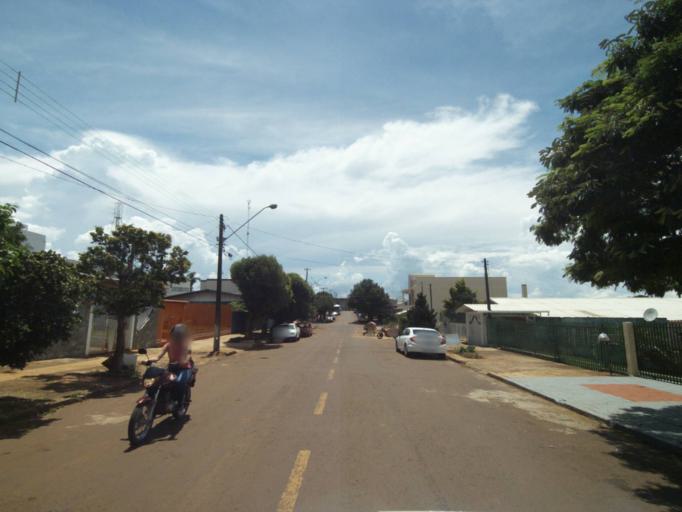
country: BR
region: Parana
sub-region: Guaraniacu
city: Guaraniacu
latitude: -25.1002
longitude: -52.8648
